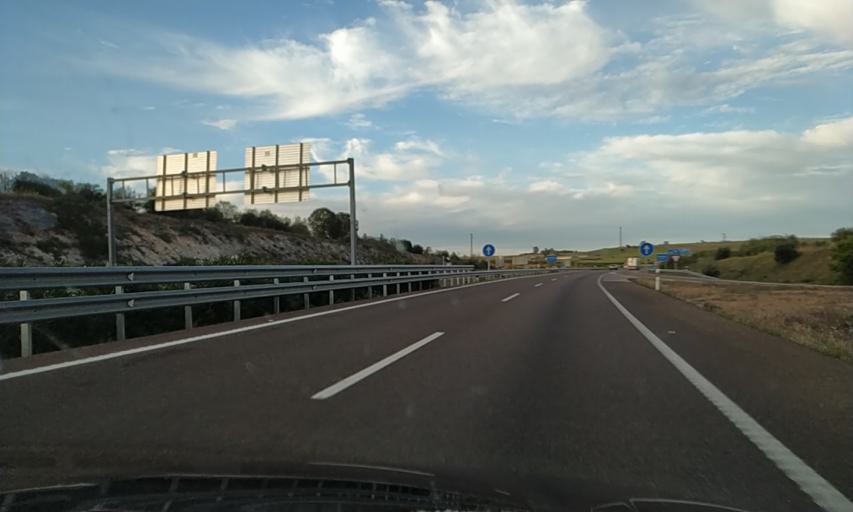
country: ES
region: Extremadura
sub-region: Provincia de Badajoz
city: Merida
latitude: 38.9386
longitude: -6.3626
